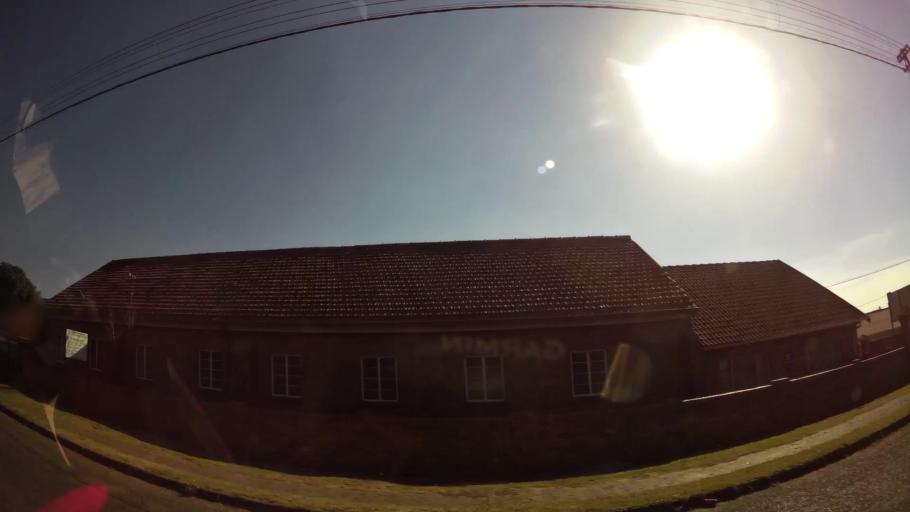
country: ZA
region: Gauteng
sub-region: City of Johannesburg Metropolitan Municipality
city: Johannesburg
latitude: -26.1892
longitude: 27.9790
